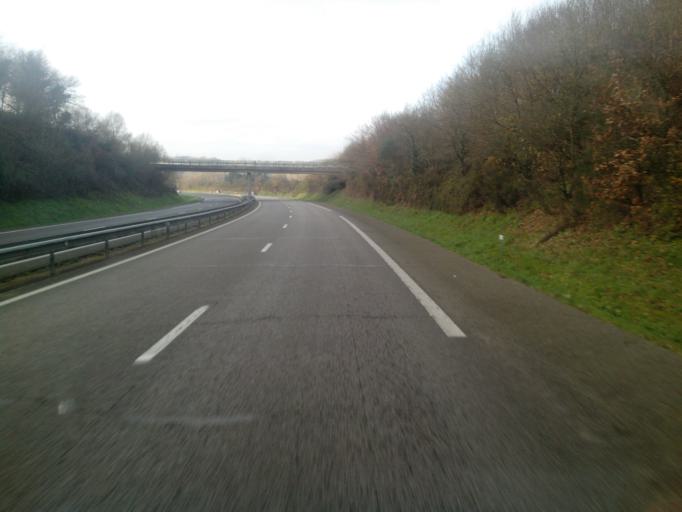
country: FR
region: Brittany
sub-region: Departement du Morbihan
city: Ploermel
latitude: 47.9315
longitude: -2.4185
